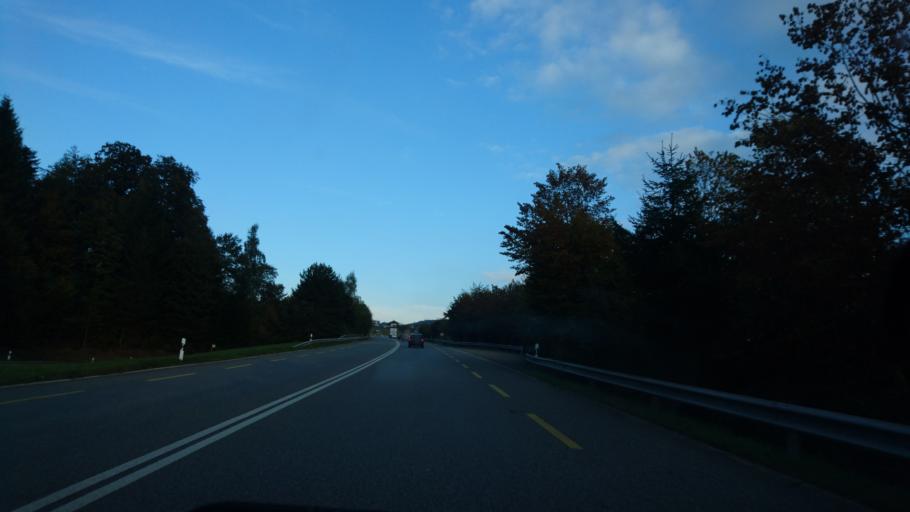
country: CH
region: Bern
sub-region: Bern-Mittelland District
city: Biglen
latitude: 46.9175
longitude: 7.6011
